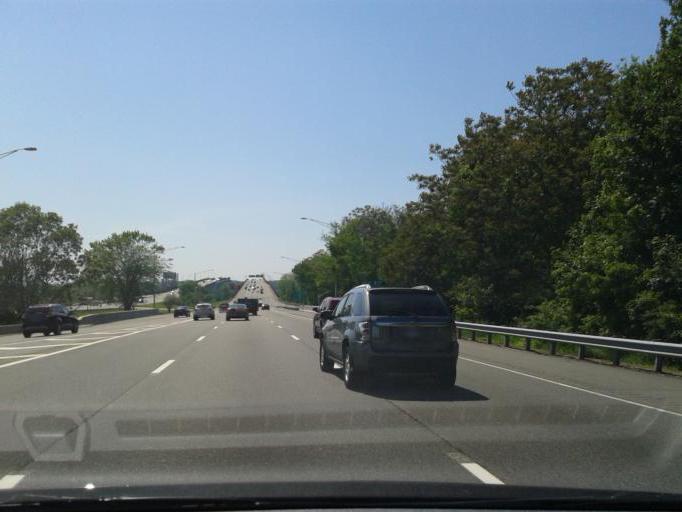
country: US
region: Connecticut
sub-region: New London County
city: Groton
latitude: 41.3650
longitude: -72.0739
